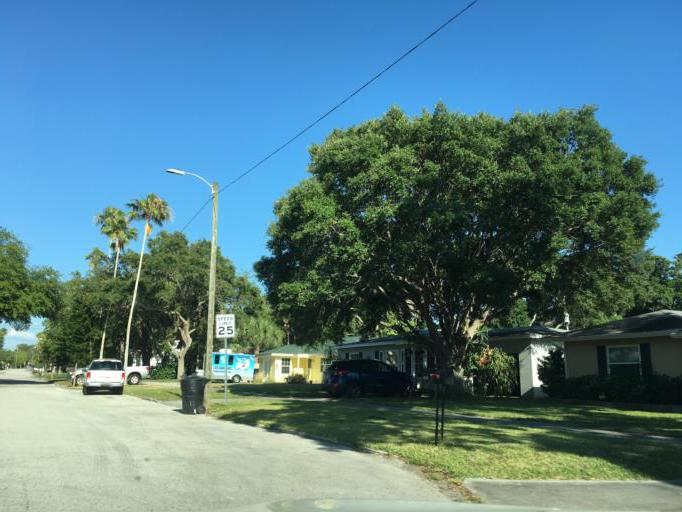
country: US
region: Florida
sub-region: Pinellas County
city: Clearwater
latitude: 27.9946
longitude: -82.7932
